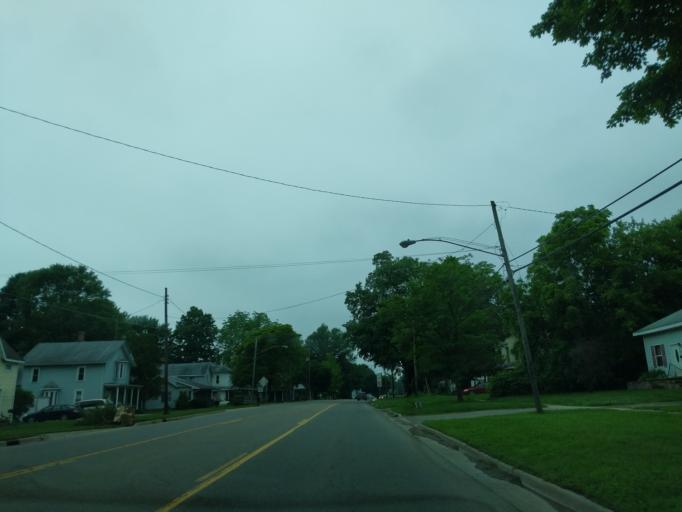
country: US
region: Michigan
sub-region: Branch County
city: Quincy
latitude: 41.9432
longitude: -84.8879
